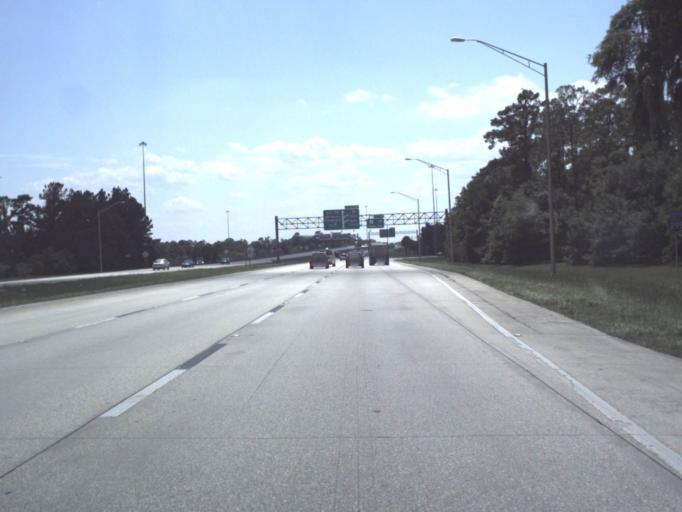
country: US
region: Florida
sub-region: Saint Johns County
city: Fruit Cove
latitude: 30.1699
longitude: -81.5333
